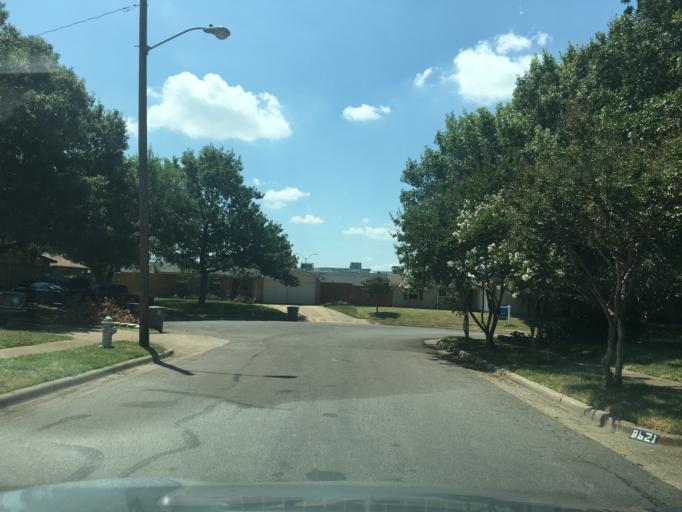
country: US
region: Texas
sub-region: Dallas County
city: Garland
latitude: 32.8664
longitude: -96.6859
